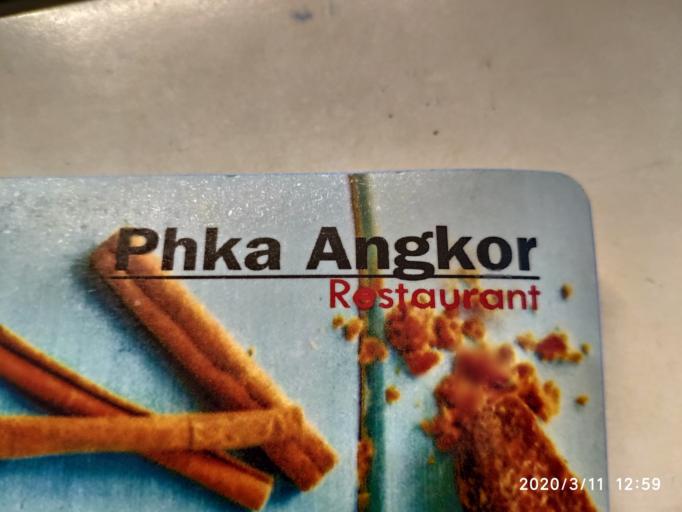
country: KH
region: Siem Reap
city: Siem Reap
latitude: 13.4332
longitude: 103.9062
